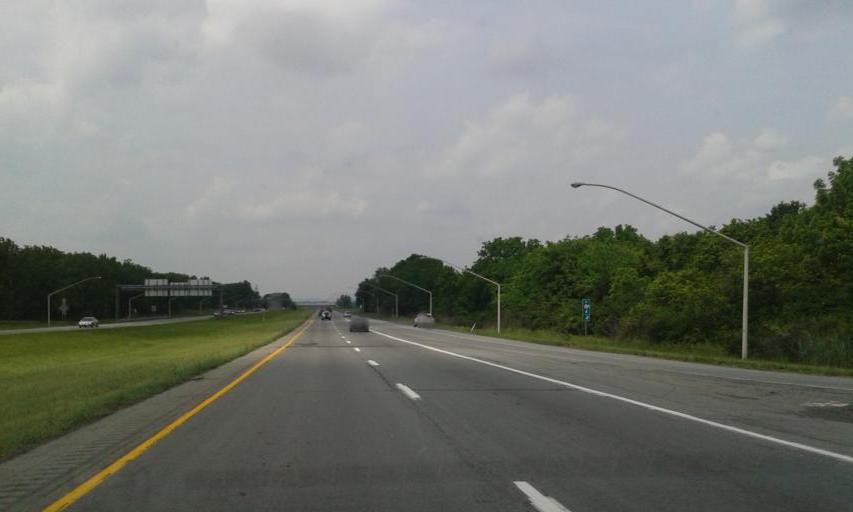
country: US
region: Pennsylvania
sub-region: Northampton County
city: Palmer Heights
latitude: 40.6869
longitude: -75.2886
